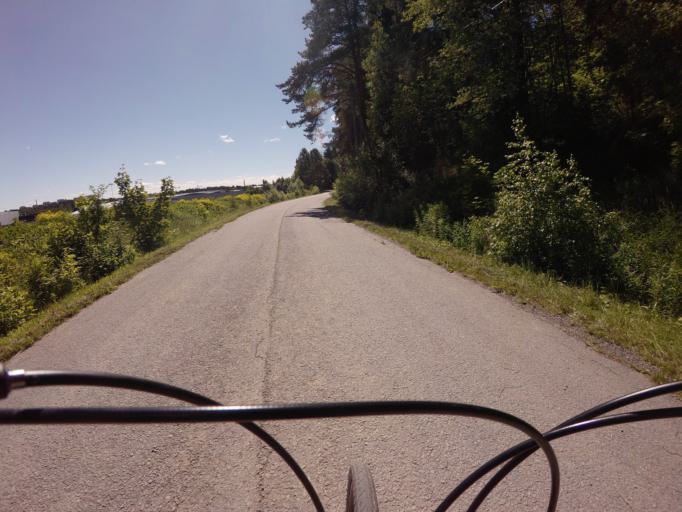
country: FI
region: Varsinais-Suomi
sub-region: Turku
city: Raisio
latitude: 60.4541
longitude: 22.2103
